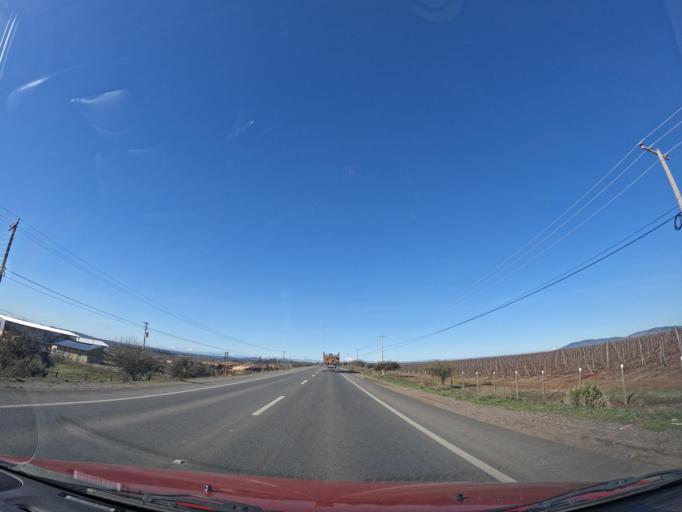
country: CL
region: Maule
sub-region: Provincia de Cauquenes
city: Cauquenes
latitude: -35.9629
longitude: -72.2433
